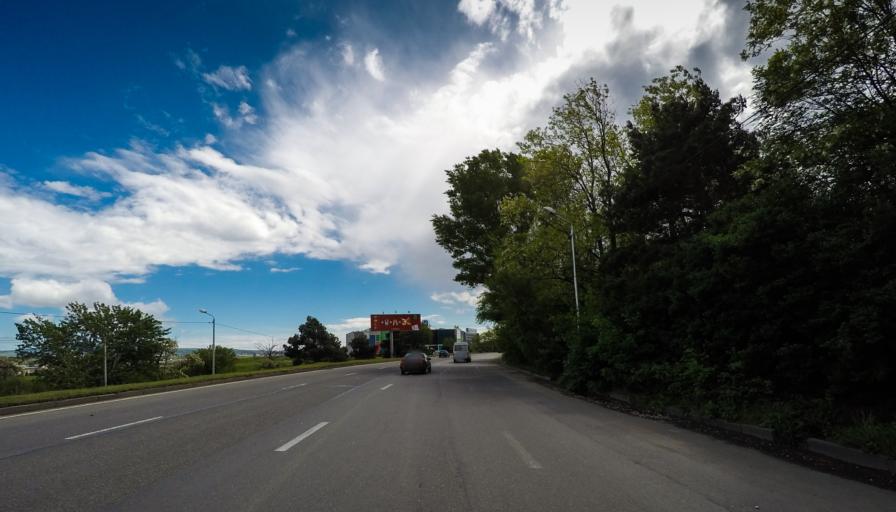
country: GE
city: Zahesi
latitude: 41.8202
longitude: 44.7709
